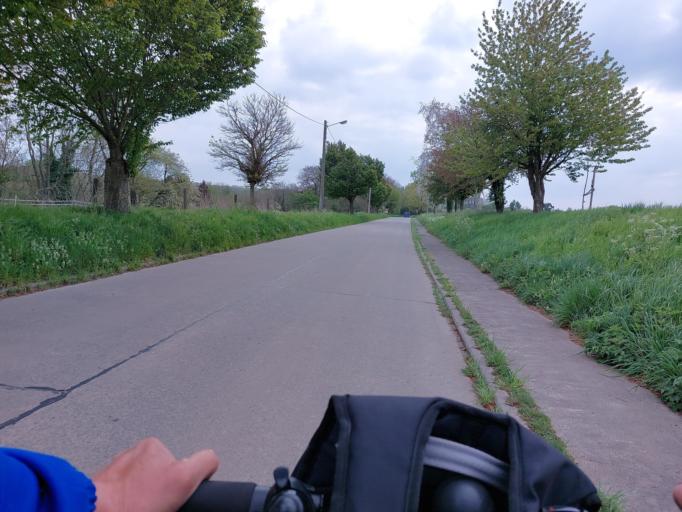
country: BE
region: Wallonia
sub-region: Province du Hainaut
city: Dour
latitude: 50.3680
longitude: 3.7286
